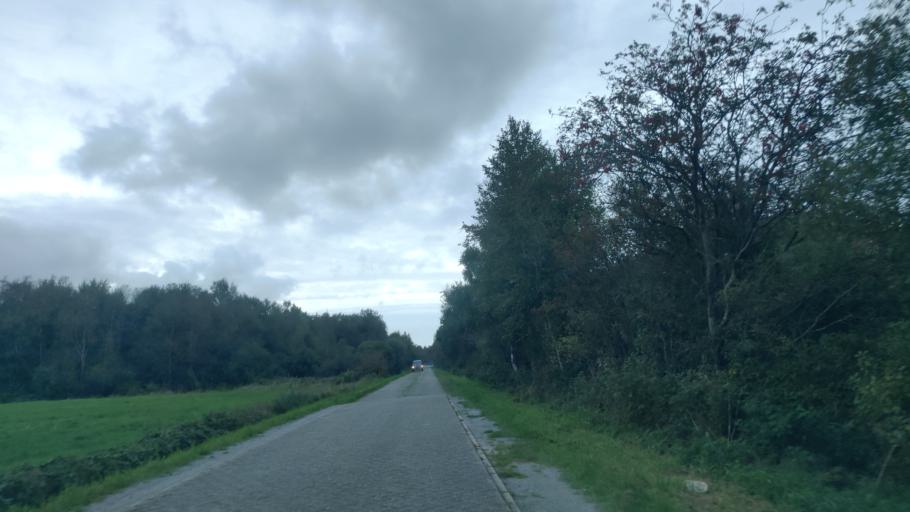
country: DE
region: Lower Saxony
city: Aurich
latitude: 53.4900
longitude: 7.4217
